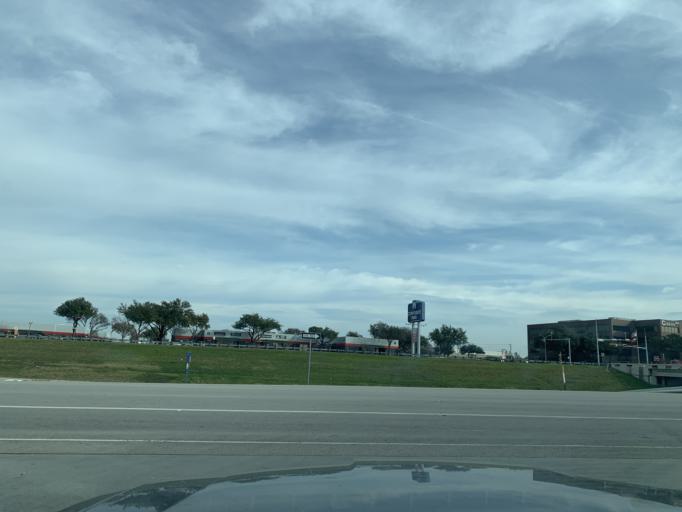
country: US
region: Texas
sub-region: Tarrant County
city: Euless
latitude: 32.7865
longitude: -97.0598
